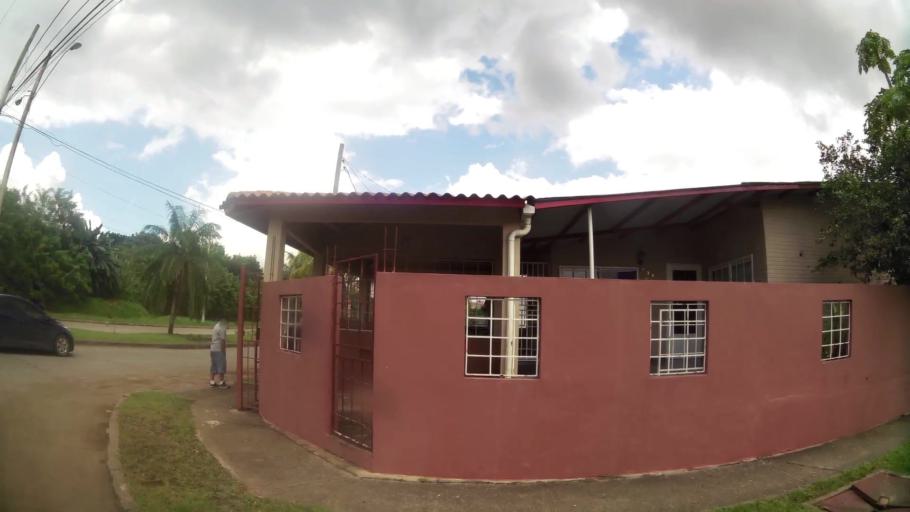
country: PA
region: Panama
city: Nuevo Arraijan
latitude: 8.9312
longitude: -79.7382
